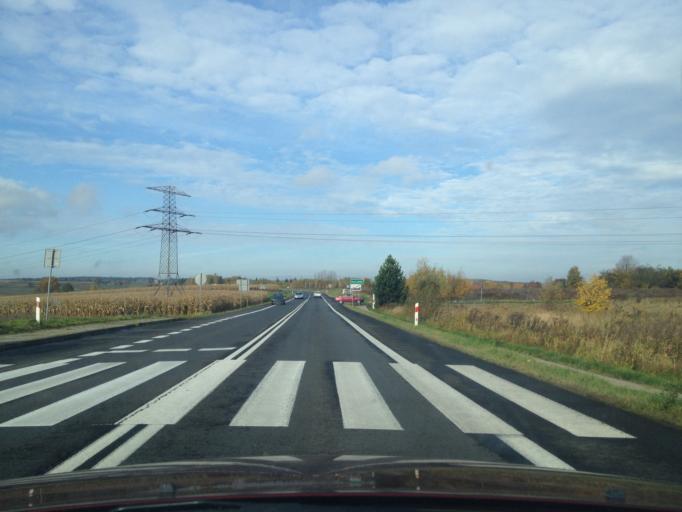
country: PL
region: Lower Silesian Voivodeship
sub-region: Powiat lubanski
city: Pisarzowice
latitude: 51.1390
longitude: 15.2354
